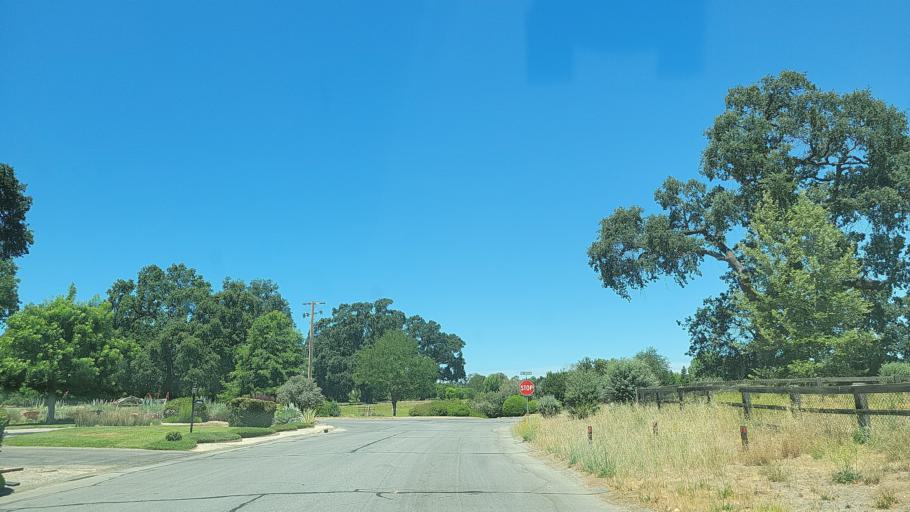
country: US
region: California
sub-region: San Luis Obispo County
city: Atascadero
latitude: 35.5121
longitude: -120.6697
